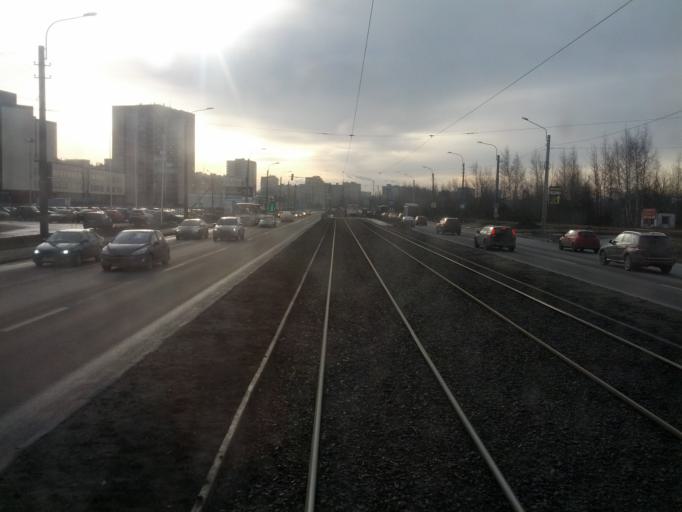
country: RU
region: St.-Petersburg
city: Obukhovo
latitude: 59.9058
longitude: 30.4526
